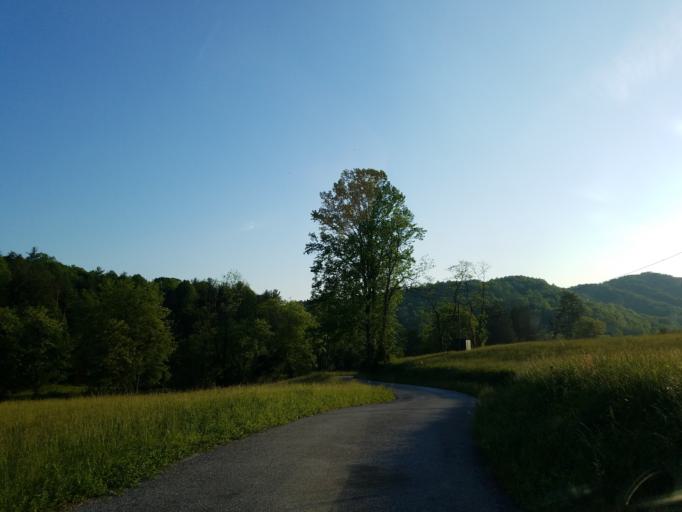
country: US
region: Georgia
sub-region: Union County
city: Blairsville
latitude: 34.7202
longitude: -84.0643
